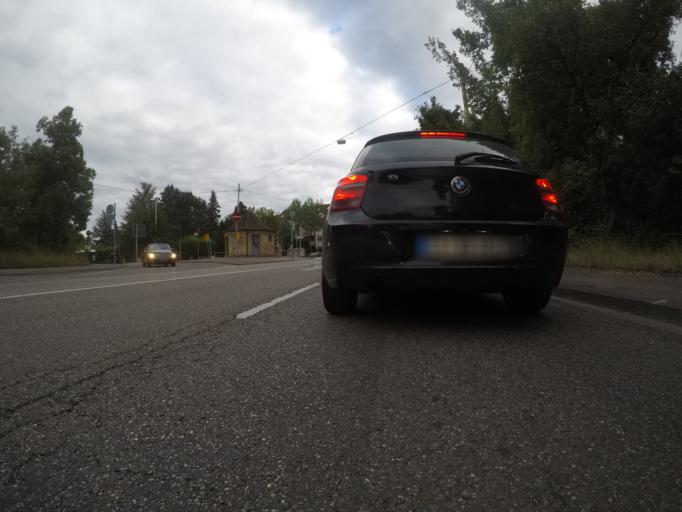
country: DE
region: Baden-Wuerttemberg
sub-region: Regierungsbezirk Stuttgart
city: Stuttgart Feuerbach
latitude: 48.7877
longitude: 9.1512
